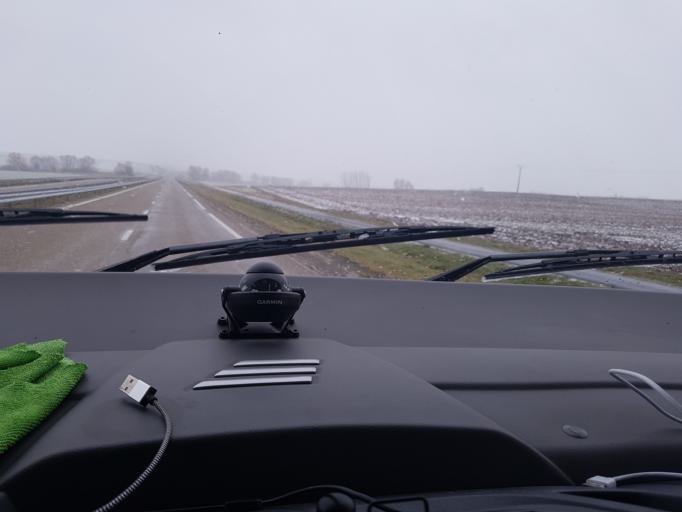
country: FR
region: Lorraine
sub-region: Departement de la Moselle
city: Dieuze
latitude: 48.7370
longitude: 6.6760
